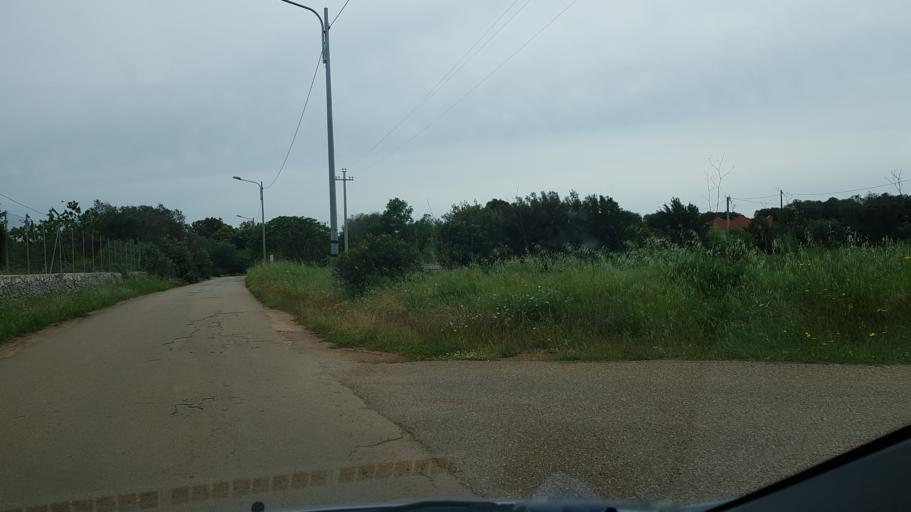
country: IT
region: Apulia
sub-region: Provincia di Brindisi
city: San Vito dei Normanni
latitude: 40.6642
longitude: 17.7388
